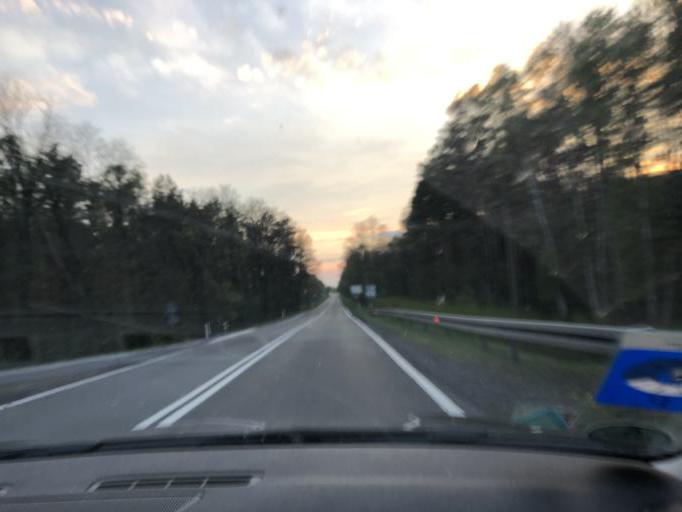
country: PL
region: Lubusz
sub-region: Powiat zarski
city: Trzebiel
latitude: 51.6355
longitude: 14.8713
